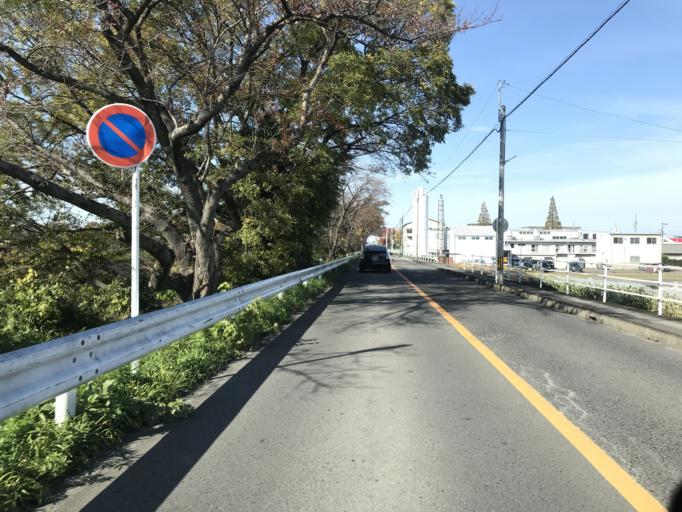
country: JP
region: Aichi
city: Iwakura
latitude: 35.2341
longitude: 136.8435
